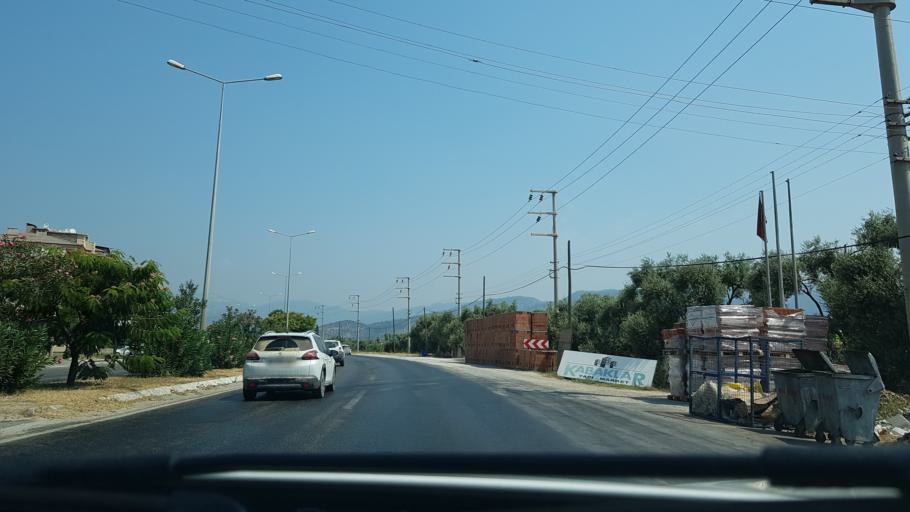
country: TR
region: Mugla
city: Milas
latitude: 37.3126
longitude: 27.7925
